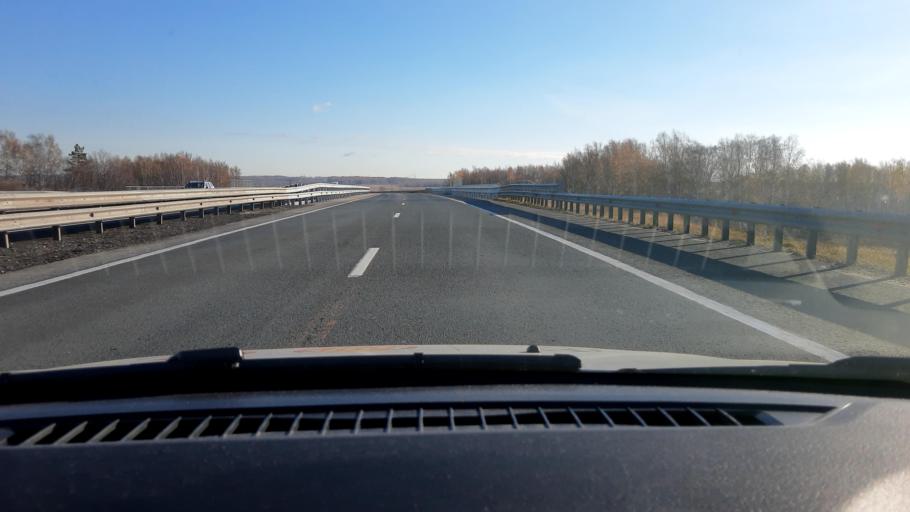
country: RU
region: Nizjnij Novgorod
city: Burevestnik
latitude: 56.1142
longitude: 43.8336
